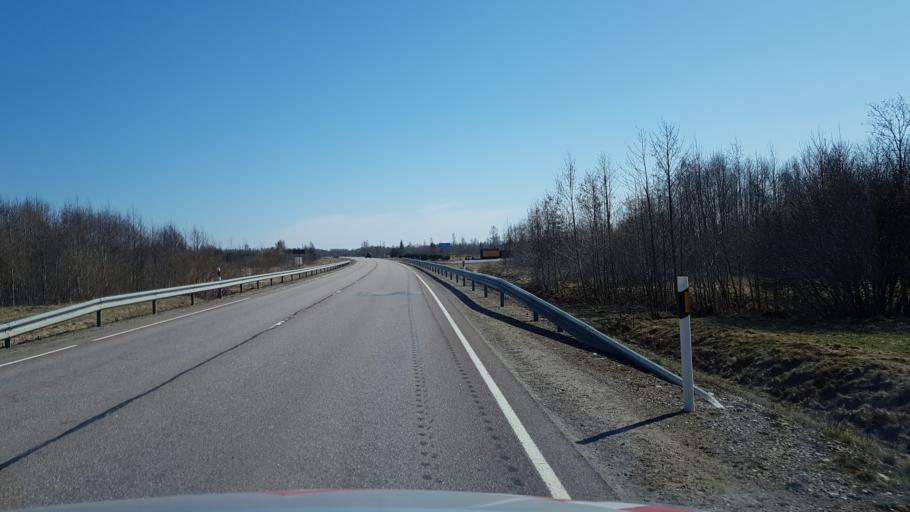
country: EE
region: Jogevamaa
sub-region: Mustvee linn
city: Mustvee
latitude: 58.8086
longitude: 26.9365
